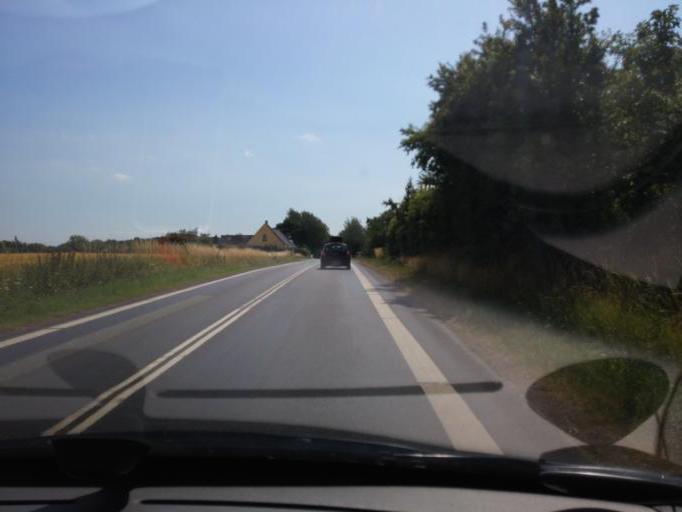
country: DK
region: South Denmark
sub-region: Langeland Kommune
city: Rudkobing
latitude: 54.8546
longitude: 10.7174
